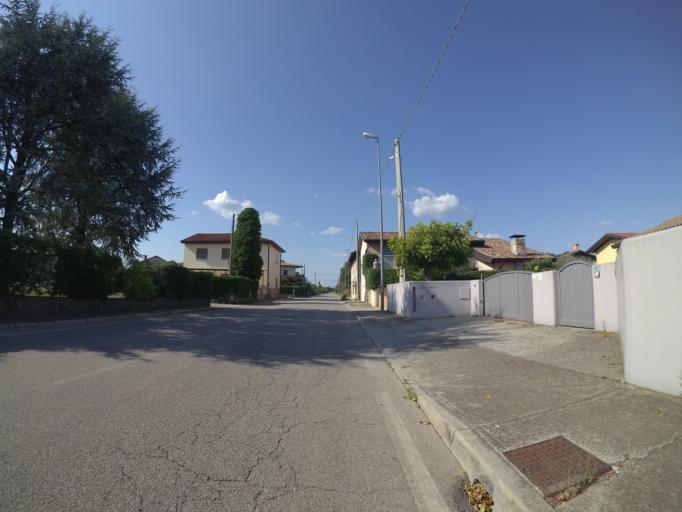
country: IT
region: Friuli Venezia Giulia
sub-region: Provincia di Udine
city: Mortegliano
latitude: 45.9517
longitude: 13.1696
